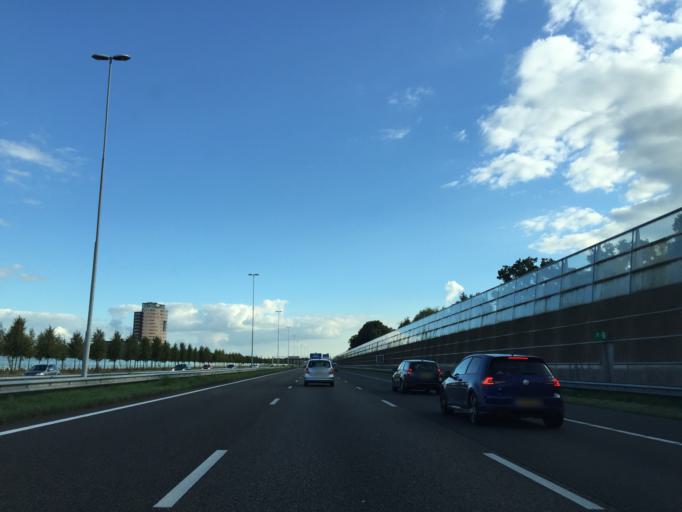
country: NL
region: North Brabant
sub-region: Gemeente Breda
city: Breda
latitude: 51.6122
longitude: 4.7155
